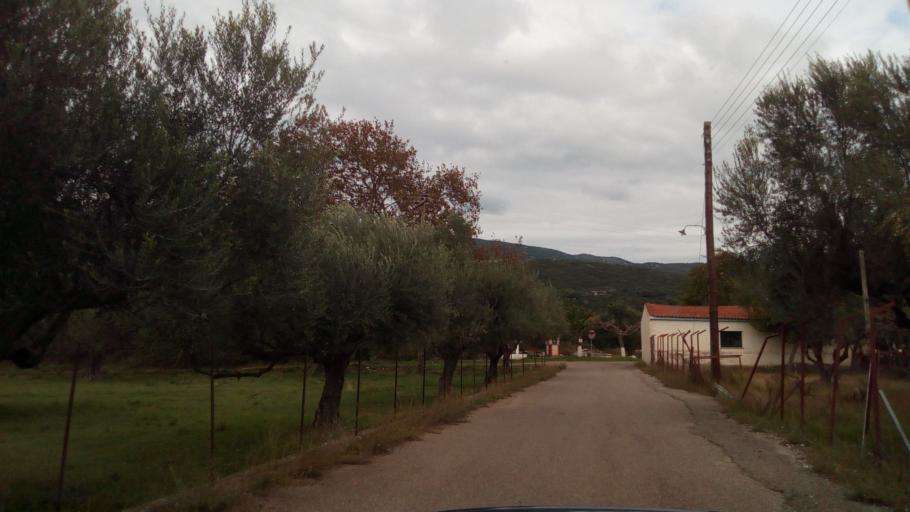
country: GR
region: West Greece
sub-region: Nomos Achaias
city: Kamarai
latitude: 38.4181
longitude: 21.9541
